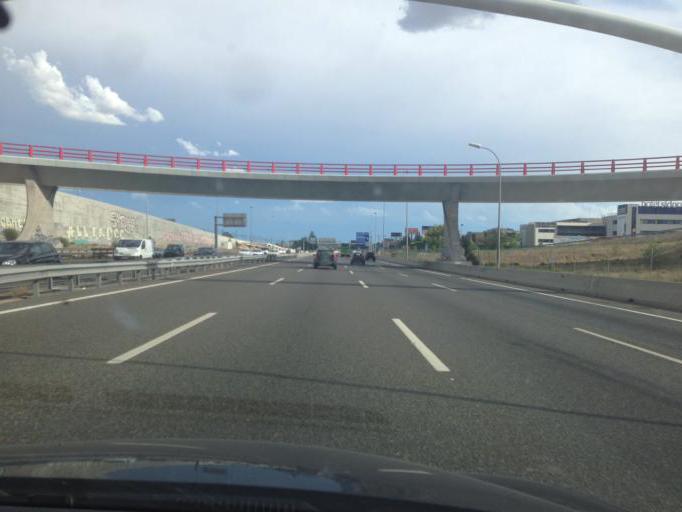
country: ES
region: Madrid
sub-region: Provincia de Madrid
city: Las Matas
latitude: 40.5475
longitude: -3.8955
